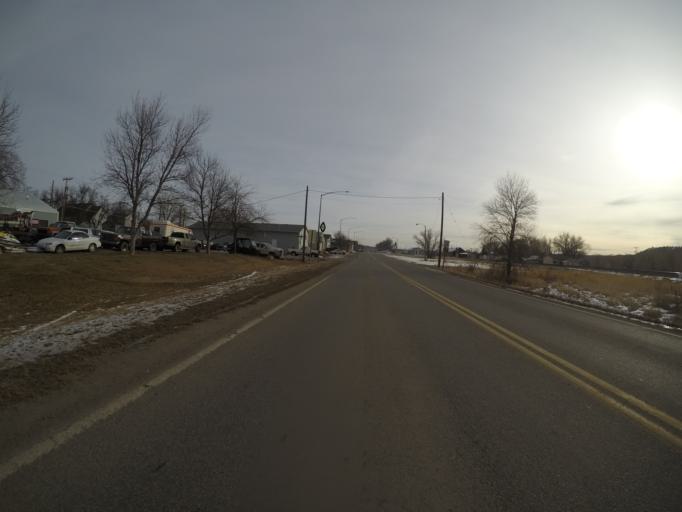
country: US
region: Montana
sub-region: Stillwater County
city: Columbus
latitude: 45.6382
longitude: -109.2585
